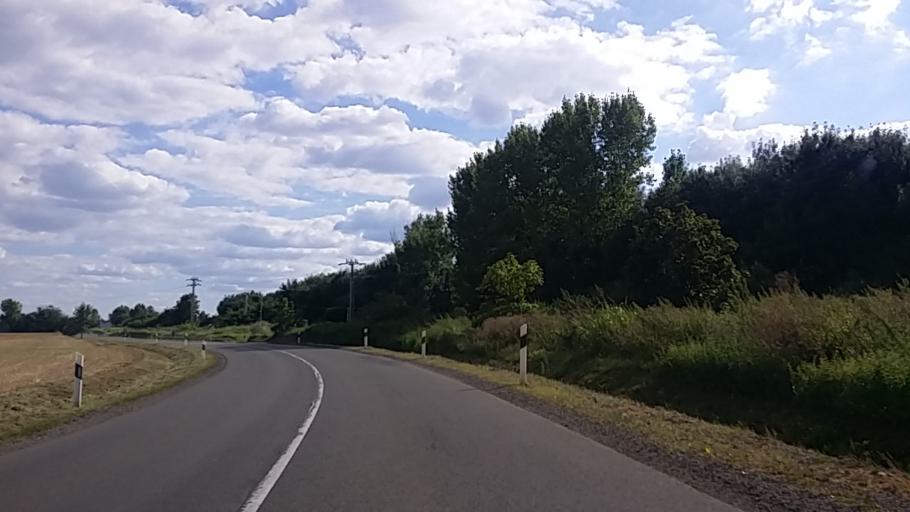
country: HU
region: Baranya
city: Sasd
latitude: 46.2722
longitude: 18.1038
